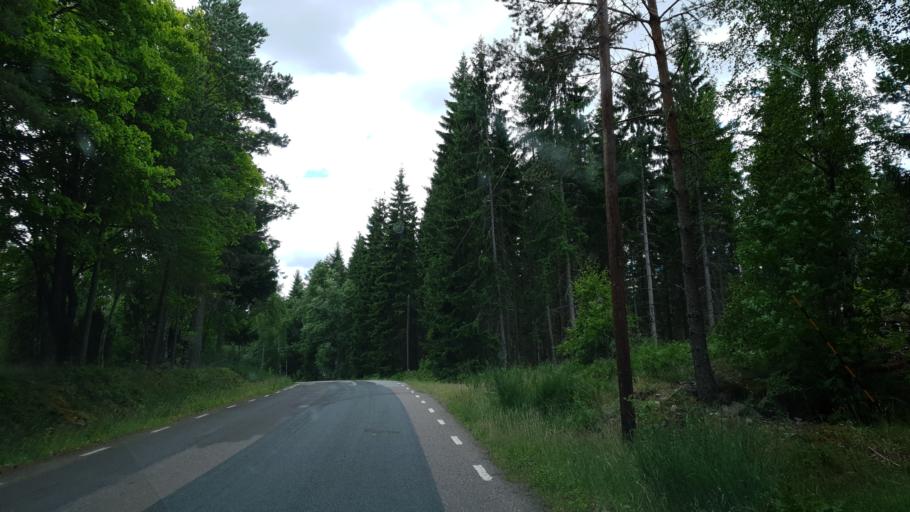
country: SE
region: Kronoberg
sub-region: Uppvidinge Kommun
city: Aseda
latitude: 57.0353
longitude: 15.5743
